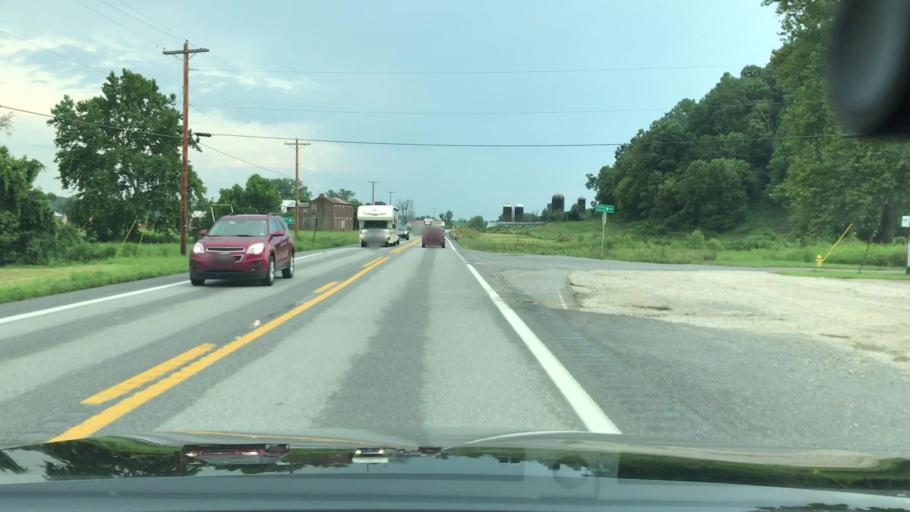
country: US
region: West Virginia
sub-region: Putnam County
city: Buffalo
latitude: 38.7170
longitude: -81.9690
